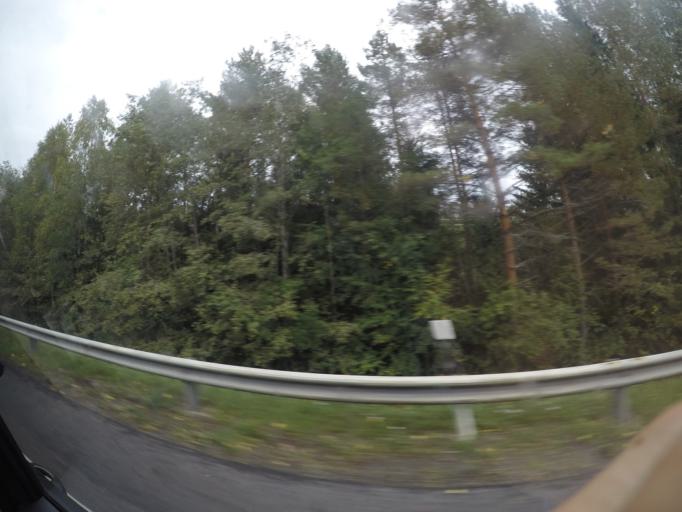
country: FI
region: Haeme
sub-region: Haemeenlinna
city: Parola
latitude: 61.1282
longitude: 24.4182
